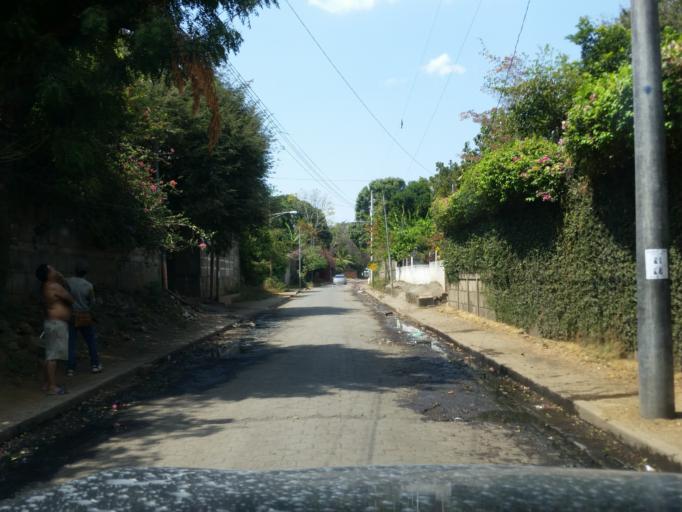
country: NI
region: Masaya
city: Ticuantepe
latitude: 12.0702
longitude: -86.2140
